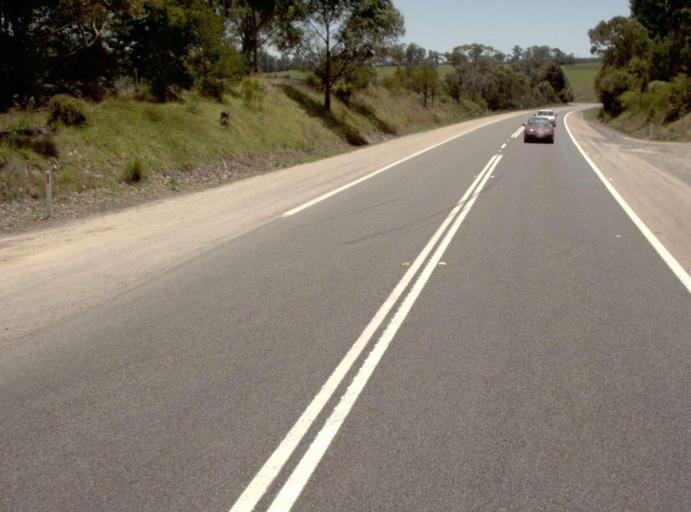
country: AU
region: Victoria
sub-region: East Gippsland
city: Lakes Entrance
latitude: -37.7052
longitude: 148.5676
